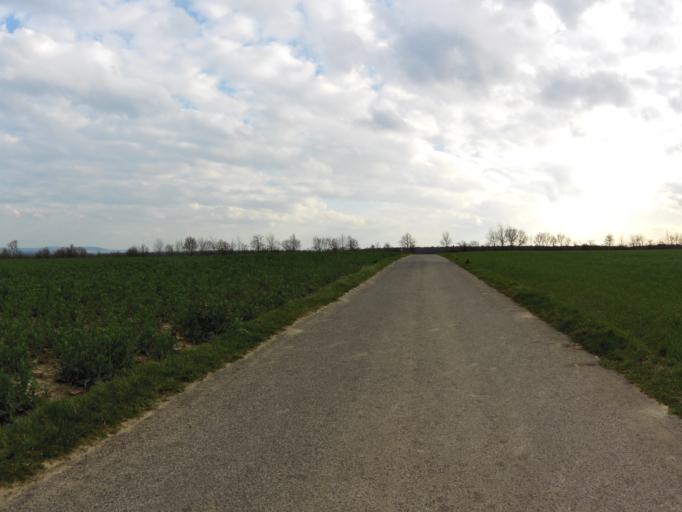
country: DE
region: Bavaria
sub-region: Regierungsbezirk Unterfranken
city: Buchbrunn
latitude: 49.7405
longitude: 10.1206
